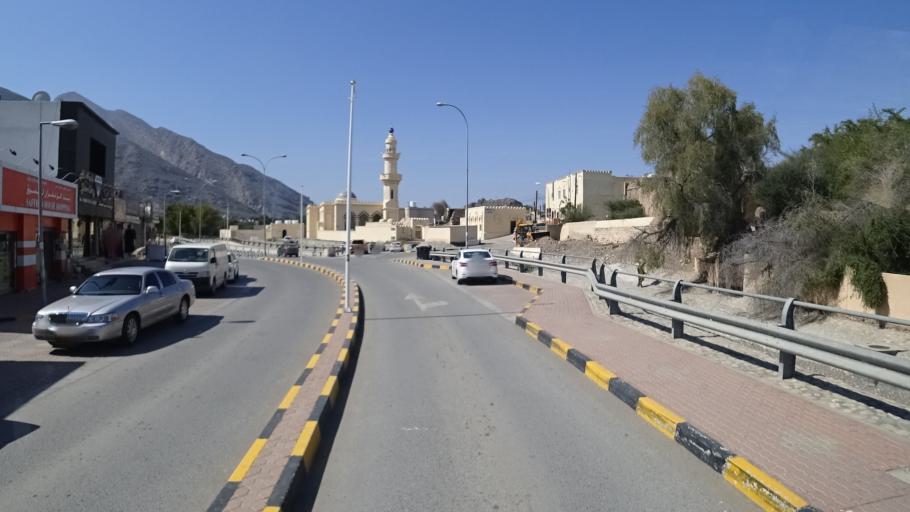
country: OM
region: Al Batinah
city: Rustaq
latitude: 23.3888
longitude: 57.4262
